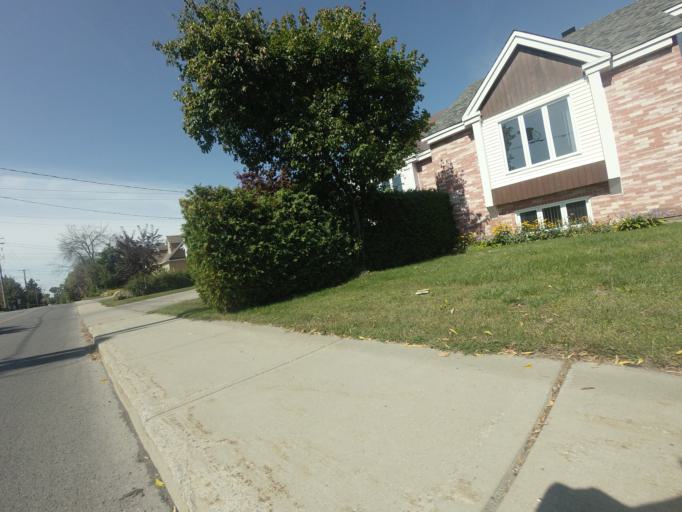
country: CA
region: Quebec
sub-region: Laurentides
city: Saint-Eustache
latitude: 45.5580
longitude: -73.9122
